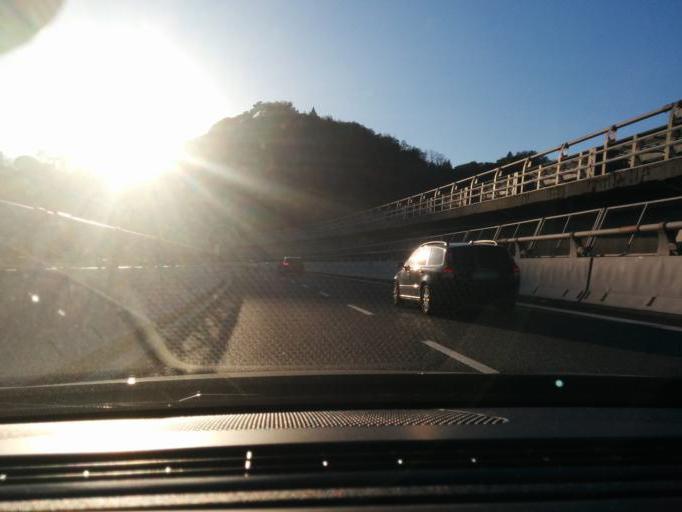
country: IT
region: Liguria
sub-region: Provincia di Genova
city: Mele
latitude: 44.4342
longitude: 8.7471
